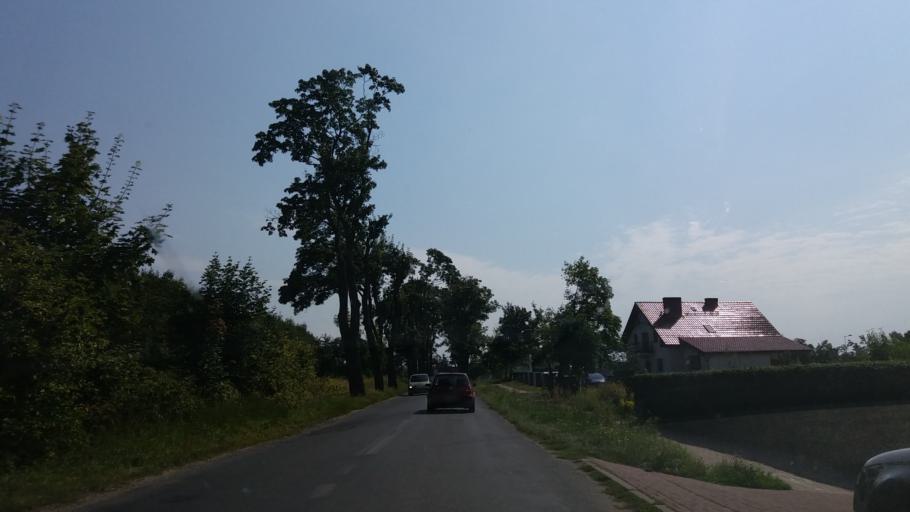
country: PL
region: Lubusz
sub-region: Powiat strzelecko-drezdenecki
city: Strzelce Krajenskie
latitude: 52.8845
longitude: 15.5192
